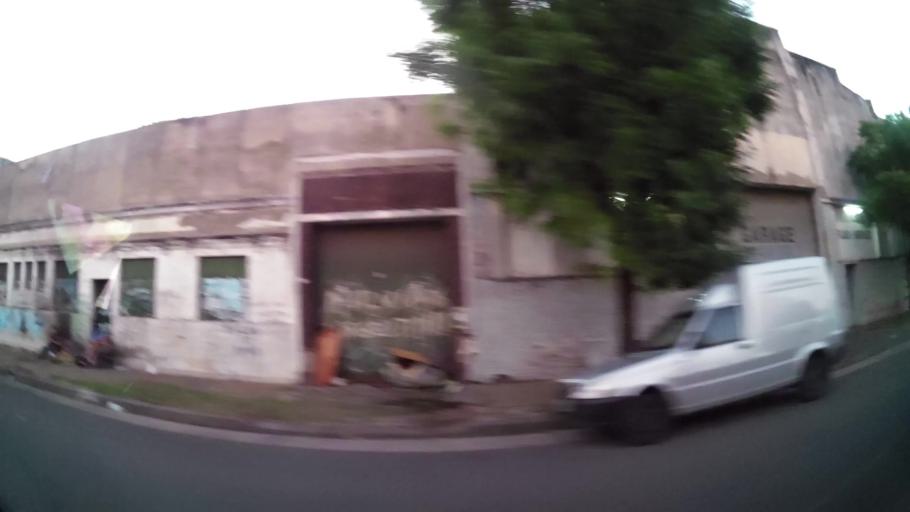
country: AR
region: Buenos Aires F.D.
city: Villa Lugano
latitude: -34.6450
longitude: -58.4338
